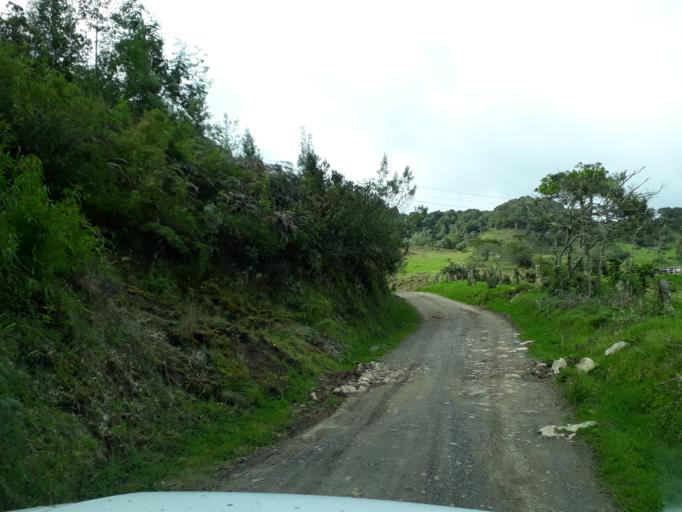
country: CO
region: Cundinamarca
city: Junin
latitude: 4.8269
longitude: -73.7675
